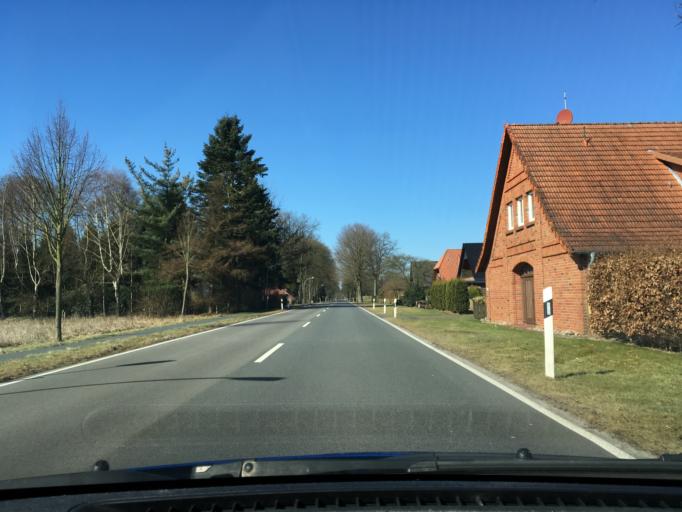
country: DE
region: Lower Saxony
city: Brockel
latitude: 53.0976
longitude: 9.5081
